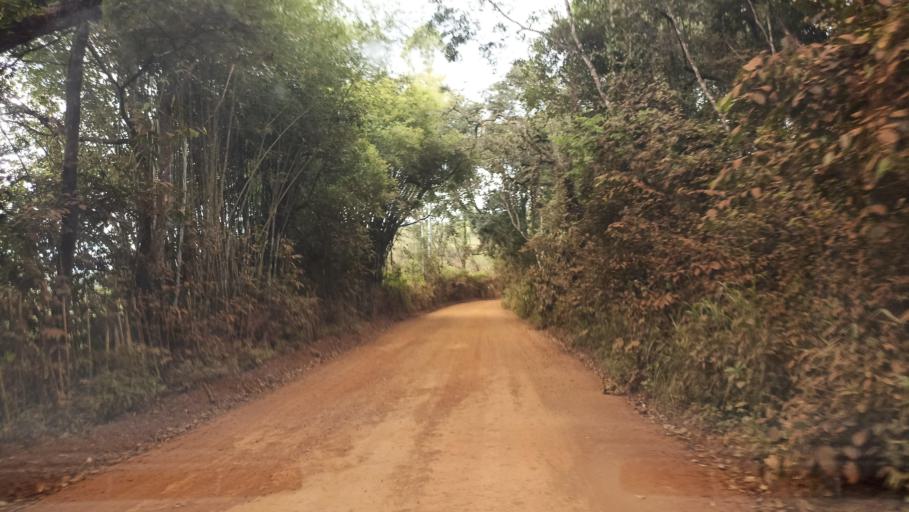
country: BR
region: Minas Gerais
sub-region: Itabirito
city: Itabirito
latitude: -20.3614
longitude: -43.7675
